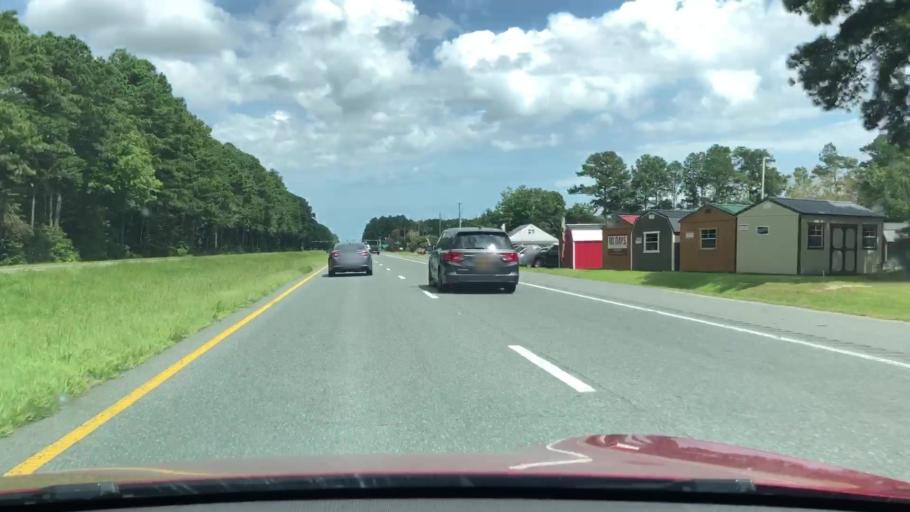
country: US
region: Virginia
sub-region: Accomack County
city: Accomac
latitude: 37.7244
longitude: -75.6781
